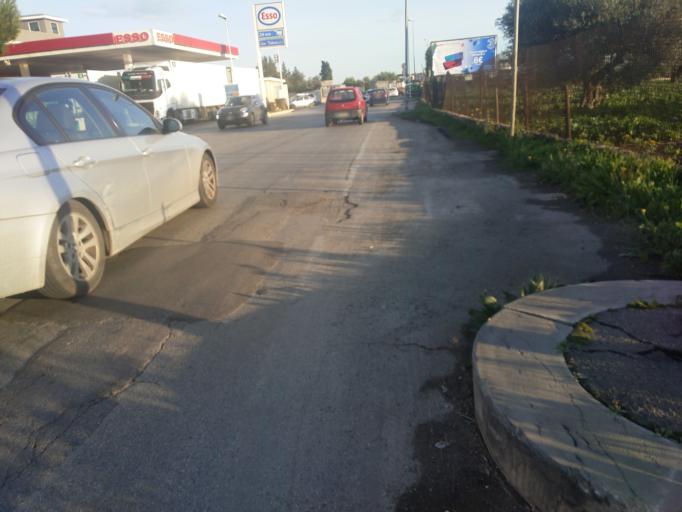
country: IT
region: Apulia
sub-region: Provincia di Bari
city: Bari
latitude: 41.1146
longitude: 16.8416
